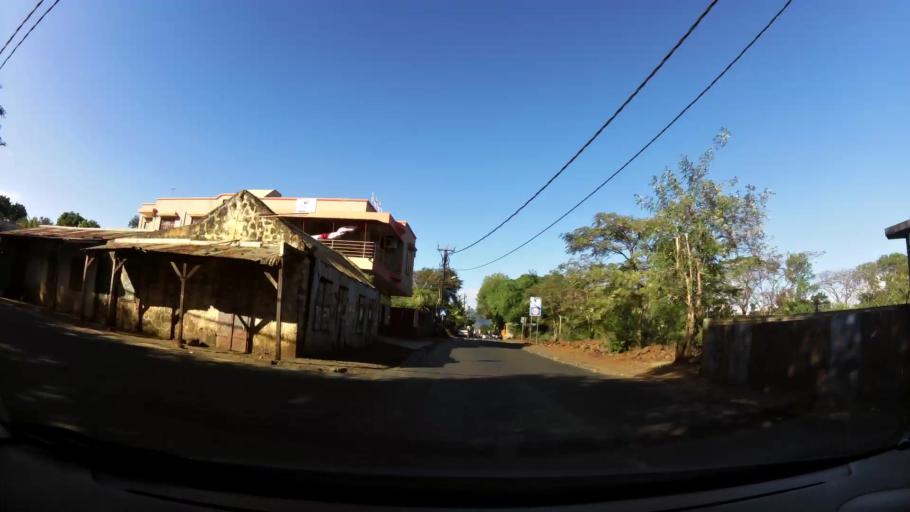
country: MU
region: Black River
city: Petite Riviere
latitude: -20.1967
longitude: 57.4427
